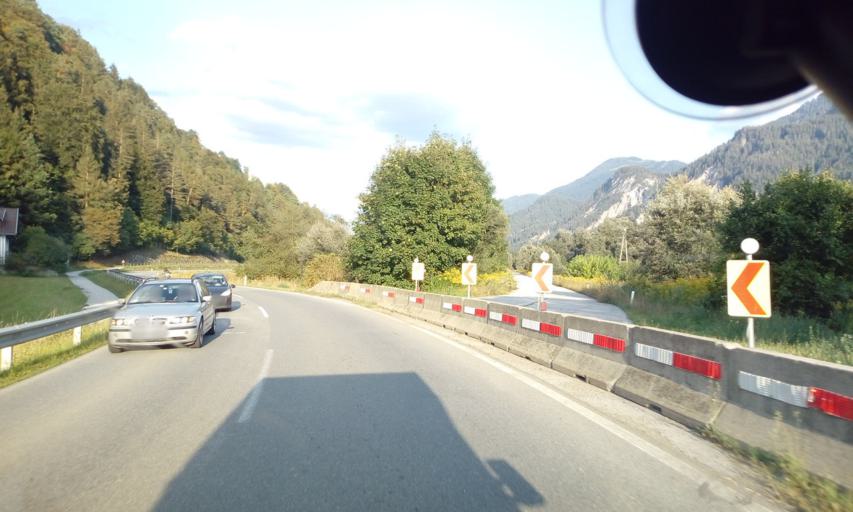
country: AT
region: Carinthia
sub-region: Politischer Bezirk Spittal an der Drau
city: Dellach im Drautal
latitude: 46.7381
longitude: 13.0685
